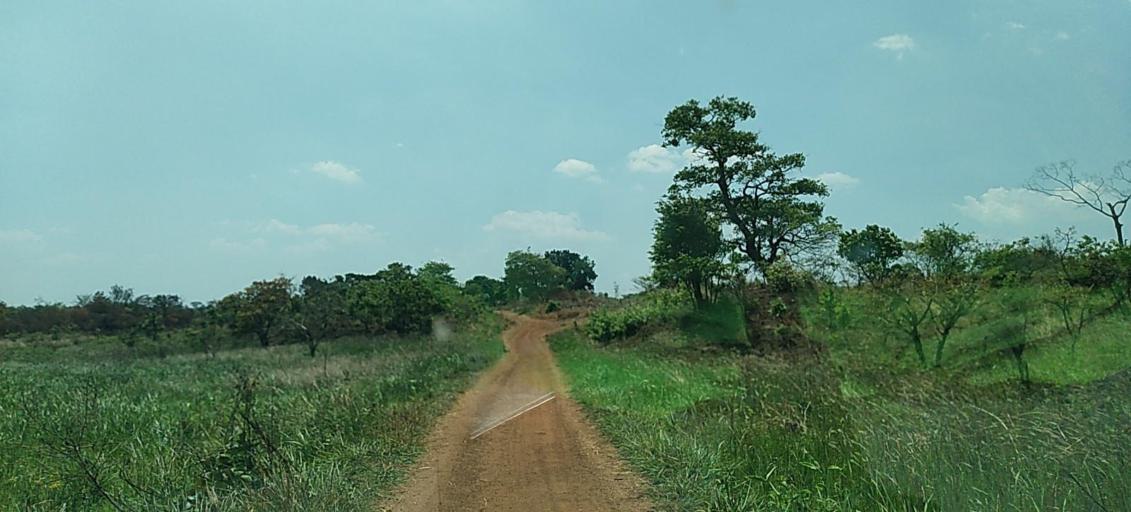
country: CD
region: Katanga
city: Kolwezi
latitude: -11.2929
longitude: 25.2089
